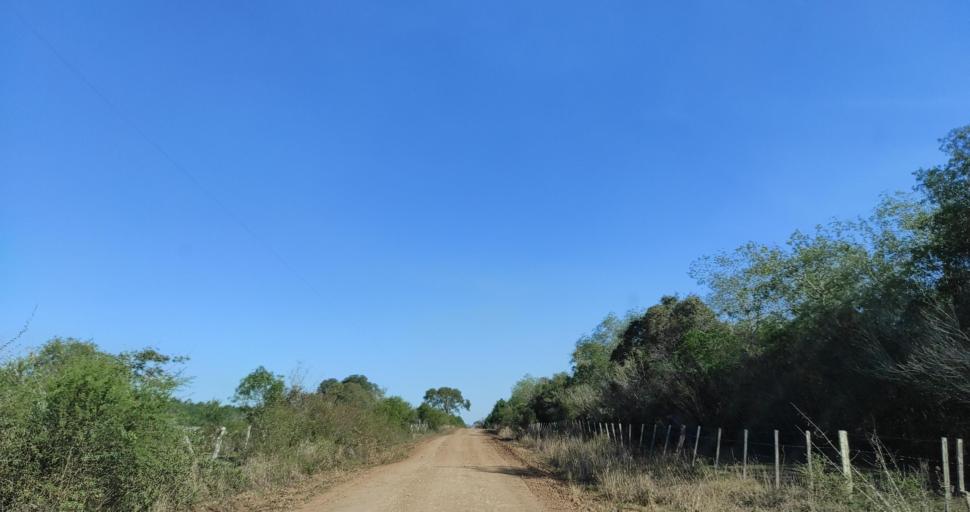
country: AR
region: Misiones
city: Cerro Cora
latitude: -27.6478
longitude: -55.6574
